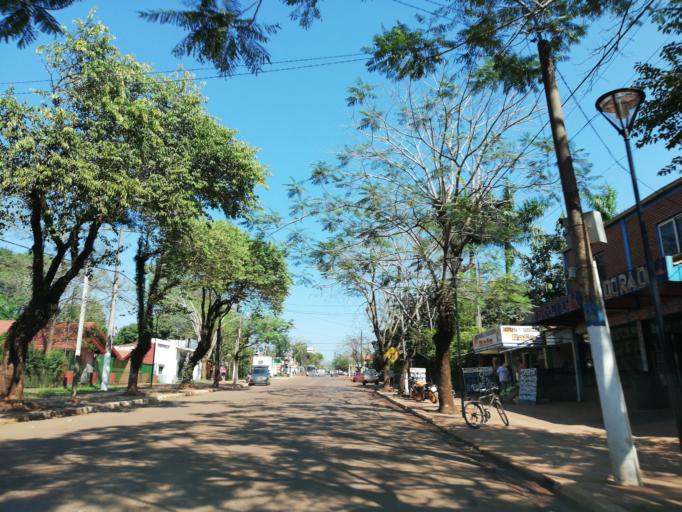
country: AR
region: Misiones
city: Puerto Eldorado
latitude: -26.4070
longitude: -54.6644
